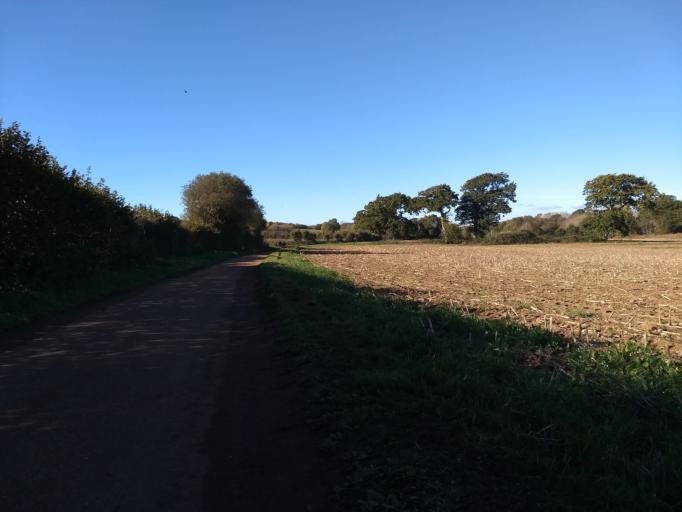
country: GB
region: England
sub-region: Isle of Wight
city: Newport
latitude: 50.6655
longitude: -1.2741
